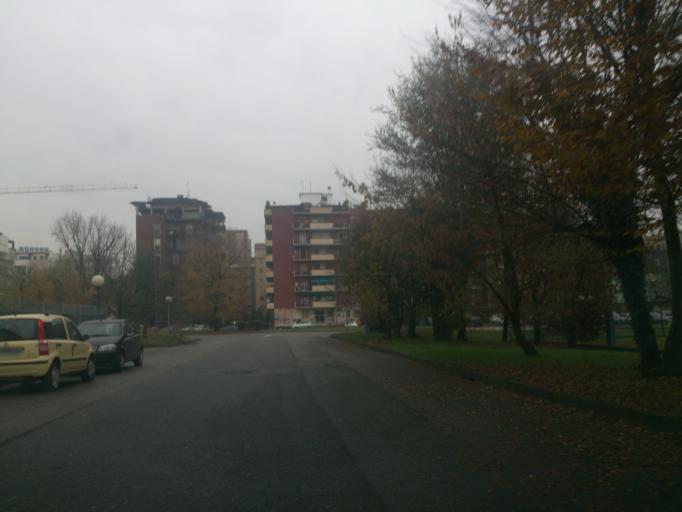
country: IT
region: Lombardy
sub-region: Citta metropolitana di Milano
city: San Donato Milanese
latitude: 45.4117
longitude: 9.2646
